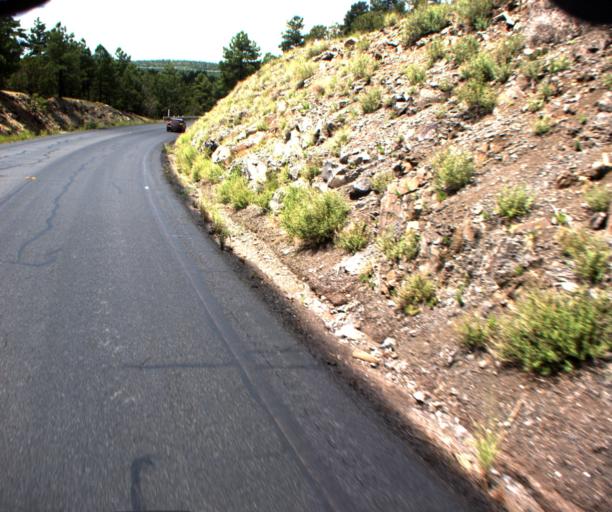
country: US
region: Arizona
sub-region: Gila County
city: Pine
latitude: 34.5170
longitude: -111.5042
